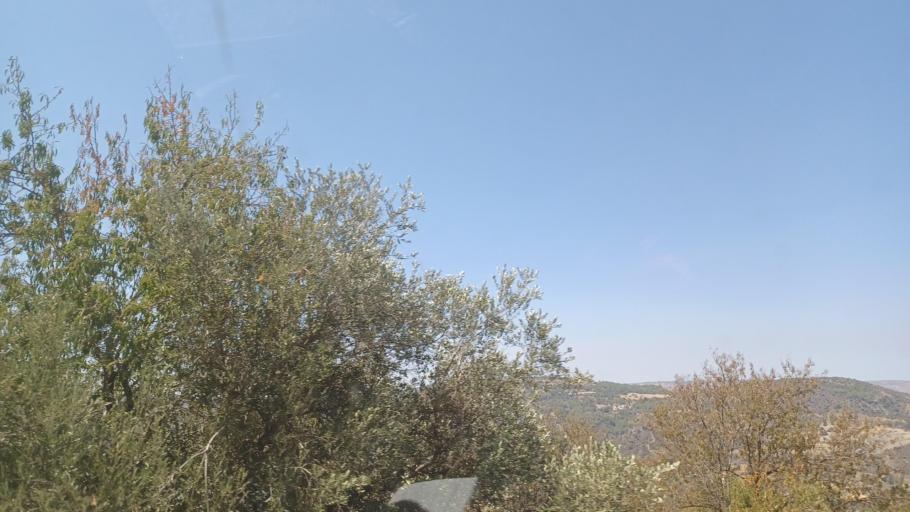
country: CY
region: Pafos
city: Polis
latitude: 35.0327
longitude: 32.5033
